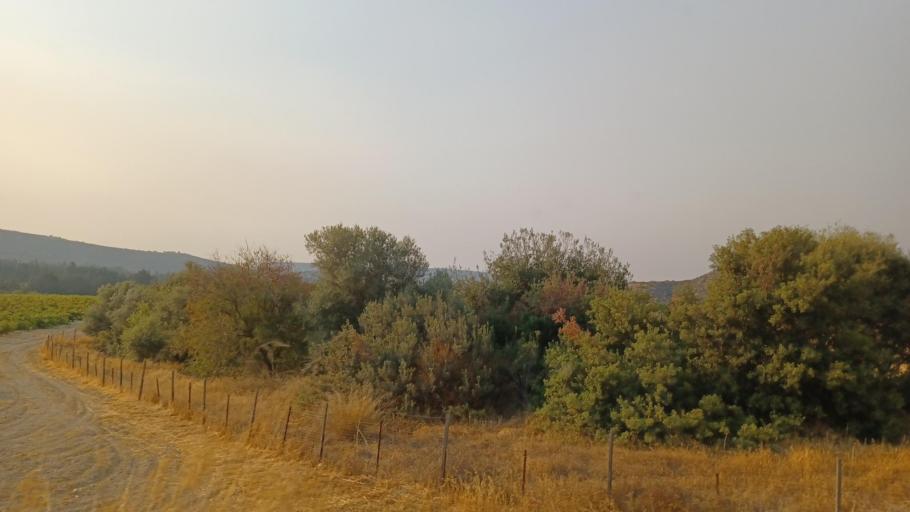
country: CY
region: Limassol
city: Pissouri
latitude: 34.7003
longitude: 32.6648
